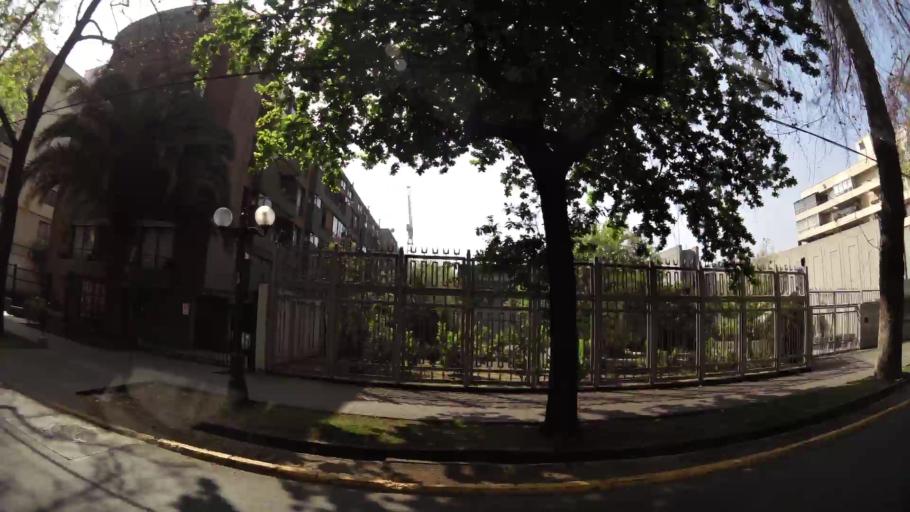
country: CL
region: Santiago Metropolitan
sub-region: Provincia de Santiago
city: Villa Presidente Frei, Nunoa, Santiago, Chile
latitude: -33.4262
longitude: -70.6082
